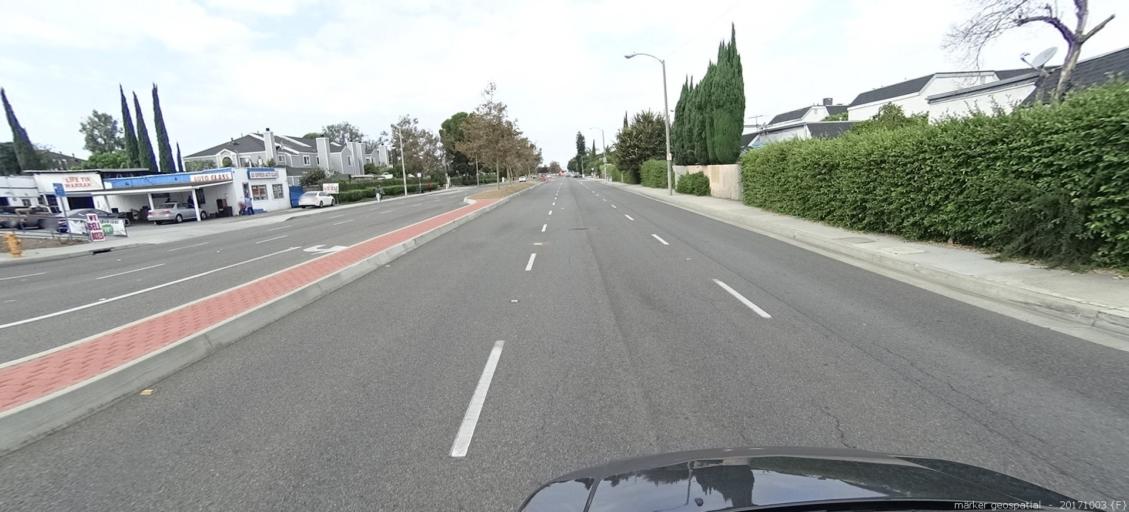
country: US
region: California
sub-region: Orange County
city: Garden Grove
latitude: 33.7597
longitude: -117.9321
